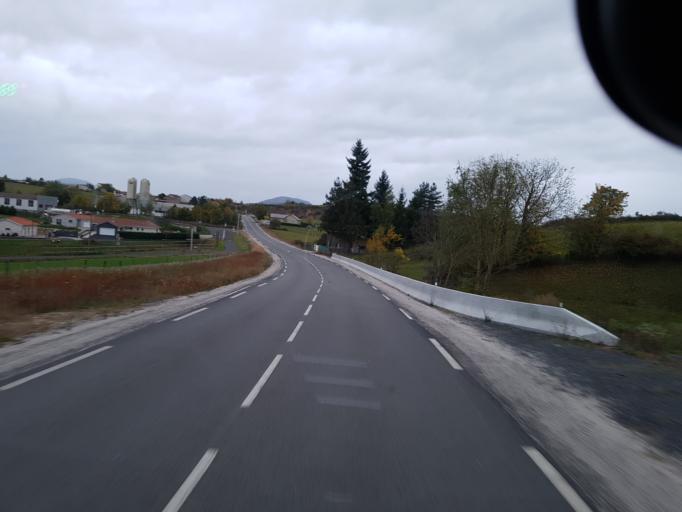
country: FR
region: Auvergne
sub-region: Departement de la Haute-Loire
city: Yssingeaux
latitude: 45.1610
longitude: 4.1416
